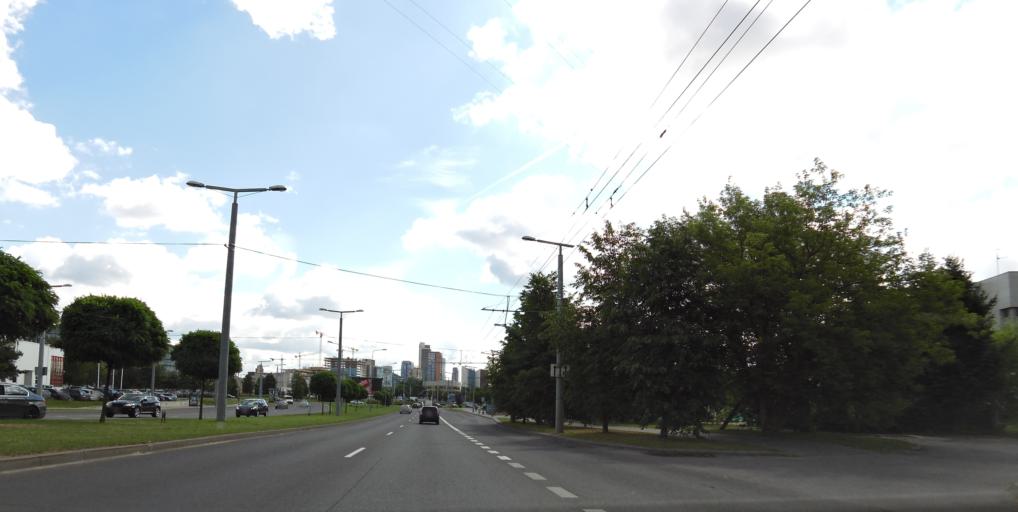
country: LT
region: Vilnius County
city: Seskine
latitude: 54.6985
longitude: 25.2597
